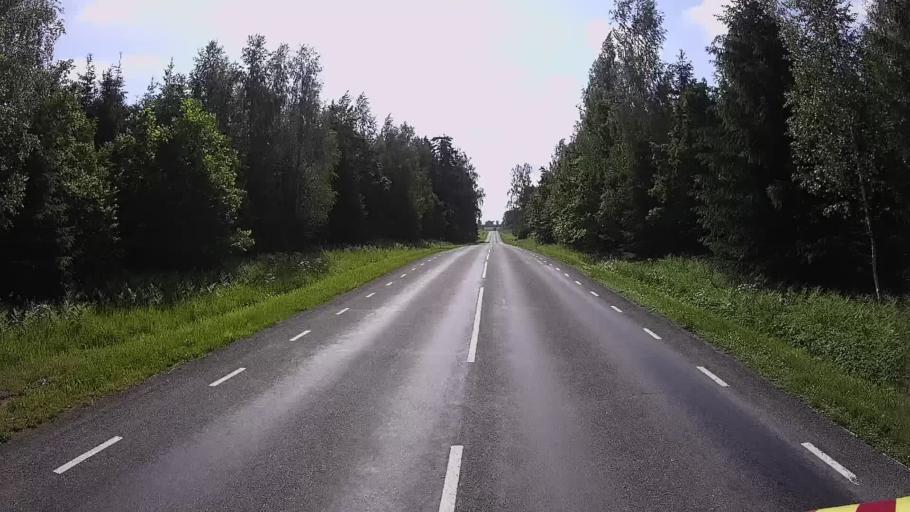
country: EE
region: Vorumaa
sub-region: Antsla vald
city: Vana-Antsla
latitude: 57.8754
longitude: 26.5871
